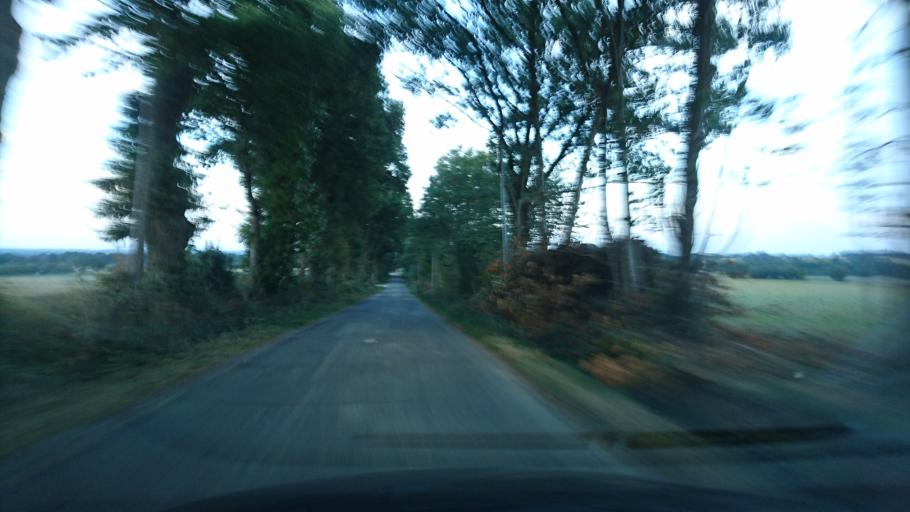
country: FR
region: Brittany
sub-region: Departement d'Ille-et-Vilaine
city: Pipriac
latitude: 47.8320
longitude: -1.9682
